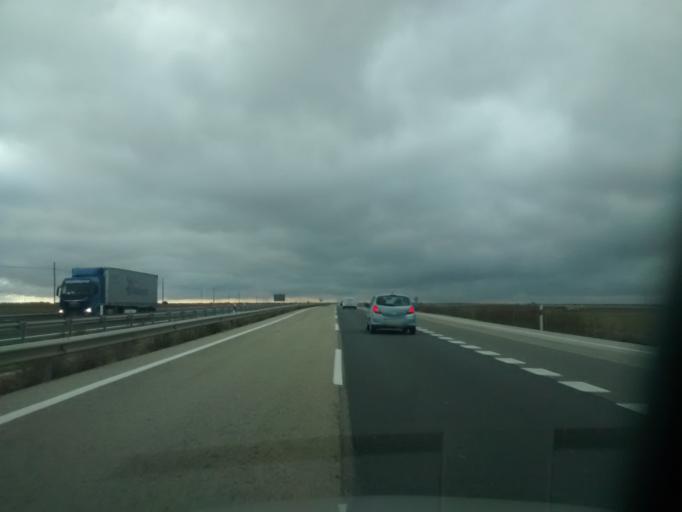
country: ES
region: Castille-La Mancha
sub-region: Provincia de Guadalajara
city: Almadrones
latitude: 40.8879
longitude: -2.7773
